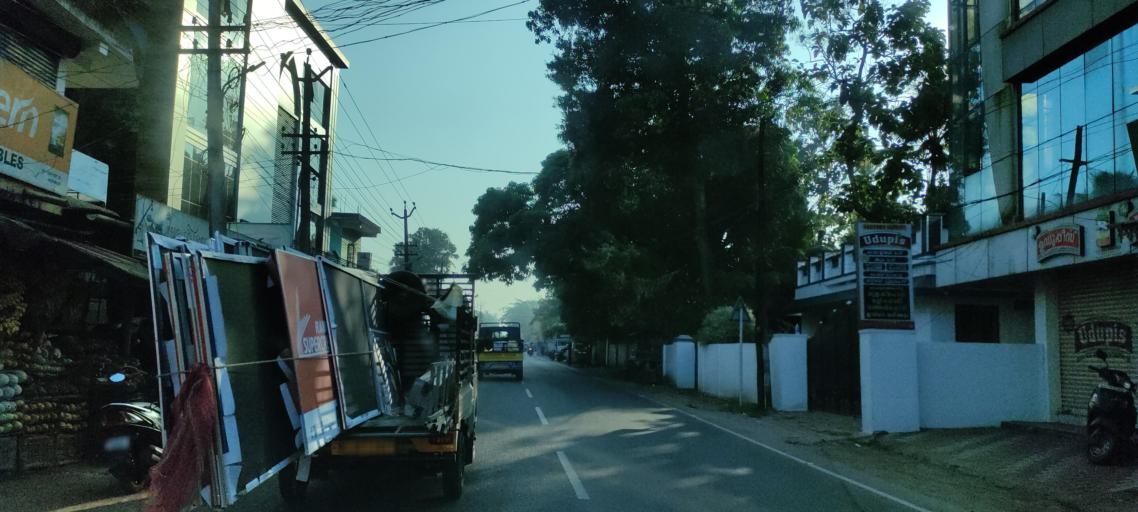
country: IN
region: Kerala
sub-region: Alappuzha
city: Kattanam
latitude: 9.1773
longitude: 76.5286
